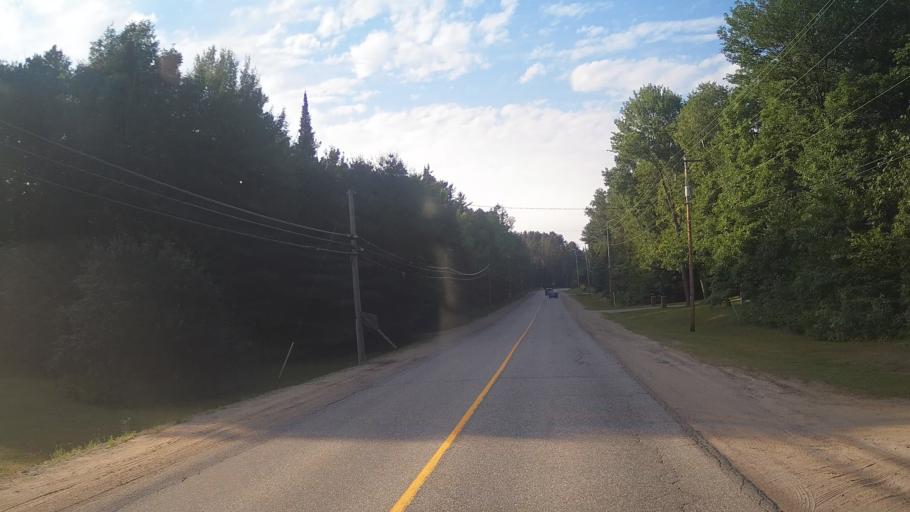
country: CA
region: Ontario
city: Huntsville
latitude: 45.3600
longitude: -79.2042
